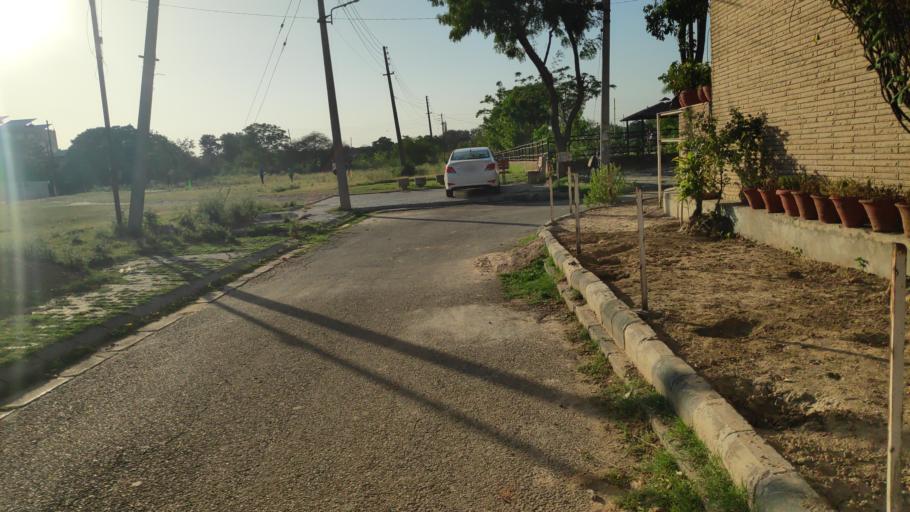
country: IN
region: Chandigarh
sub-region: Chandigarh
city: Chandigarh
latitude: 30.7230
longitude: 76.7523
